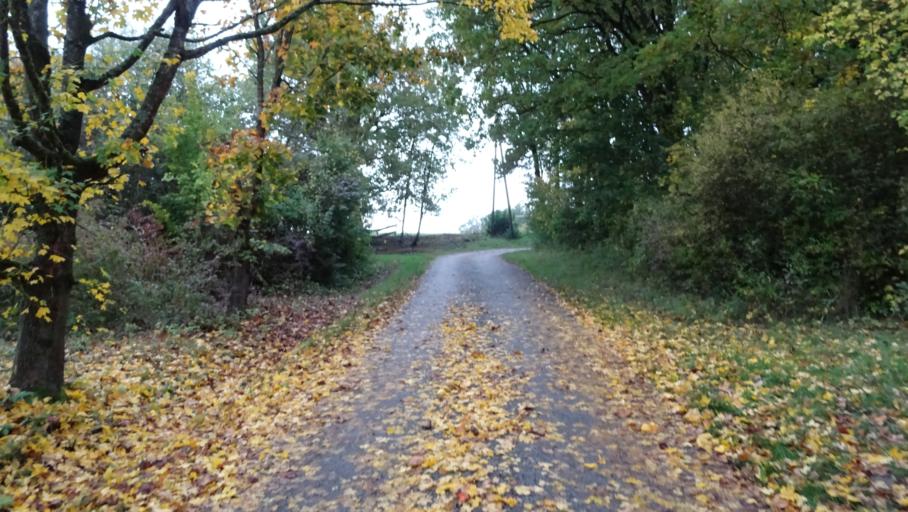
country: DE
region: Baden-Wuerttemberg
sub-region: Karlsruhe Region
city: Billigheim
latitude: 49.3406
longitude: 9.2406
